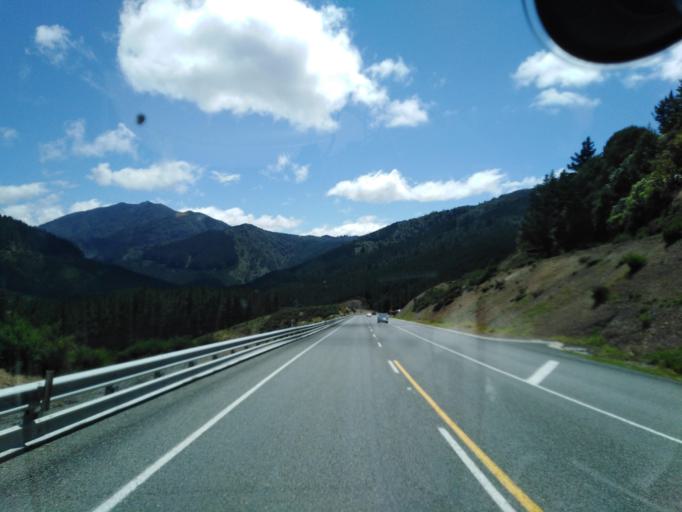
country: NZ
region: Nelson
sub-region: Nelson City
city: Nelson
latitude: -41.1877
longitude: 173.5544
